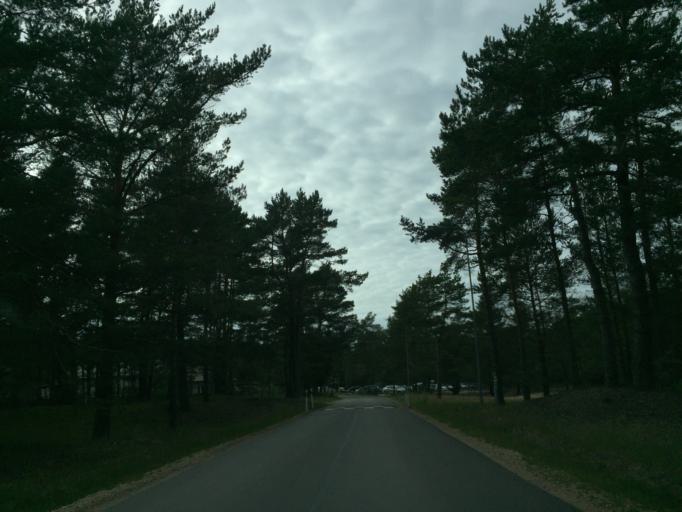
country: LV
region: Carnikava
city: Carnikava
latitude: 57.1354
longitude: 24.2481
